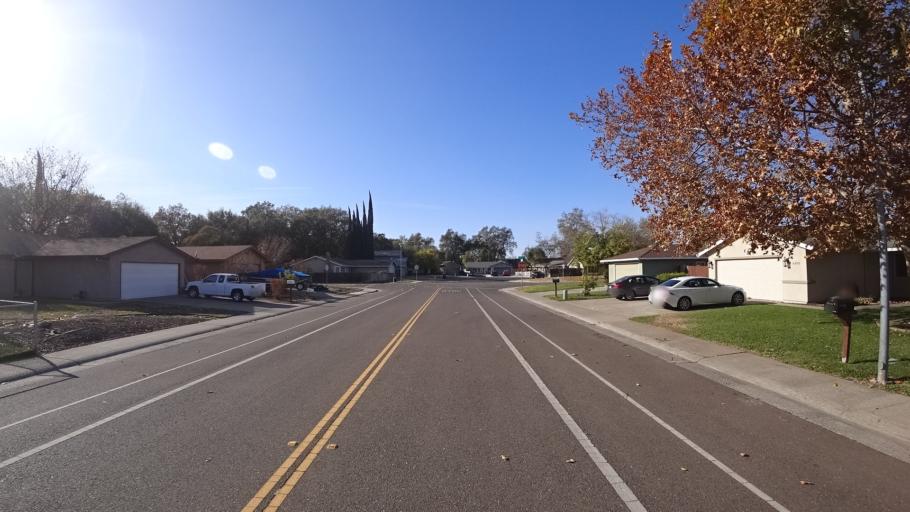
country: US
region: California
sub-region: Sacramento County
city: Antelope
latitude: 38.6991
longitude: -121.3154
